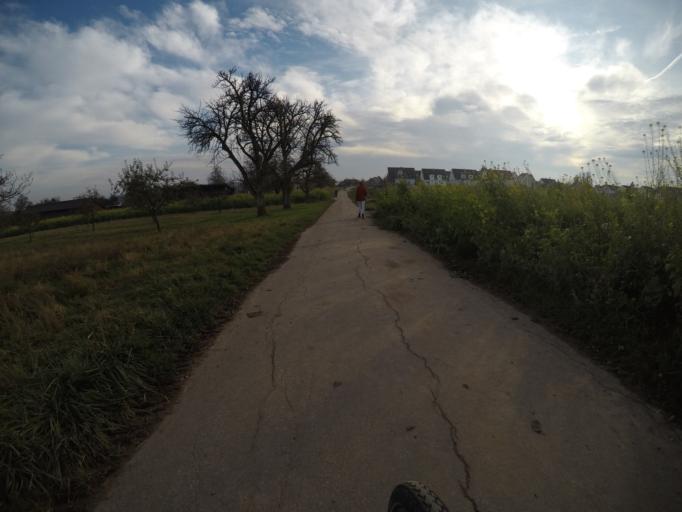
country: DE
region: Baden-Wuerttemberg
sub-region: Regierungsbezirk Stuttgart
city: Steinenbronn
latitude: 48.6979
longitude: 9.1206
